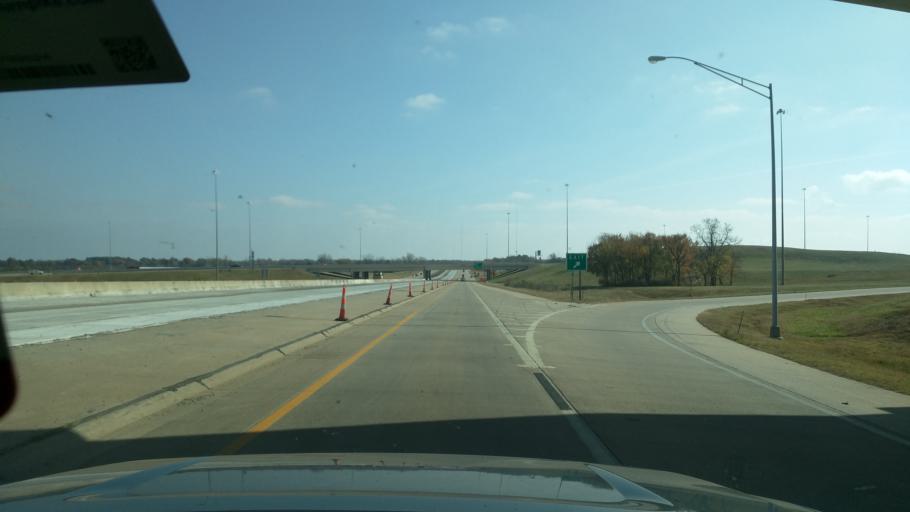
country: US
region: Oklahoma
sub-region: Tulsa County
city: Broken Arrow
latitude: 36.0478
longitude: -95.7442
